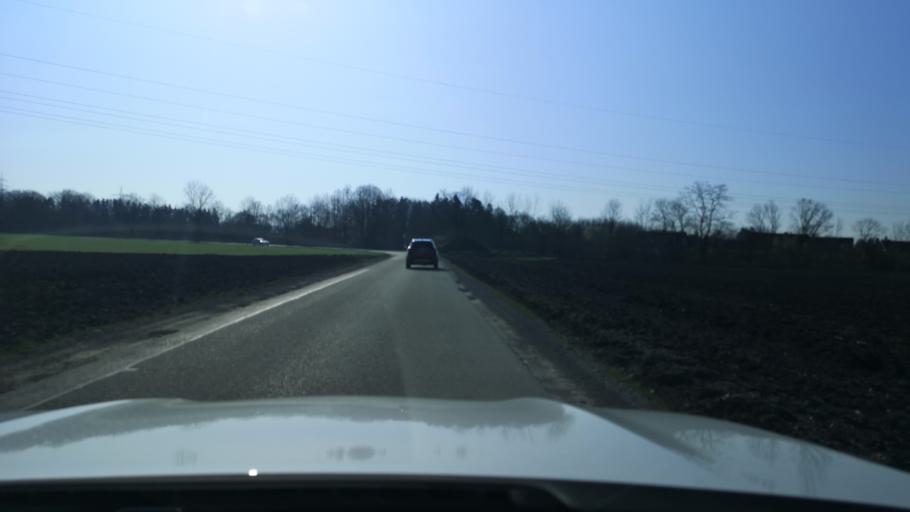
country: DE
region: Bavaria
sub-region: Upper Bavaria
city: Finsing
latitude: 48.2267
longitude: 11.8027
